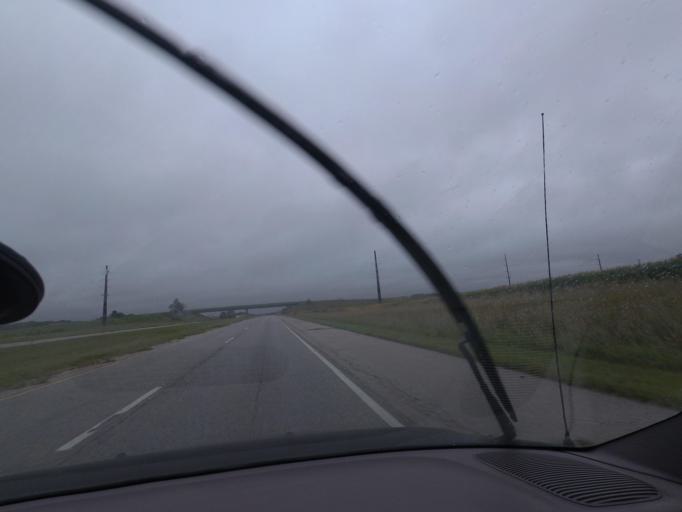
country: US
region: Illinois
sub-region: Pike County
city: Pittsfield
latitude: 39.6711
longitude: -90.8024
